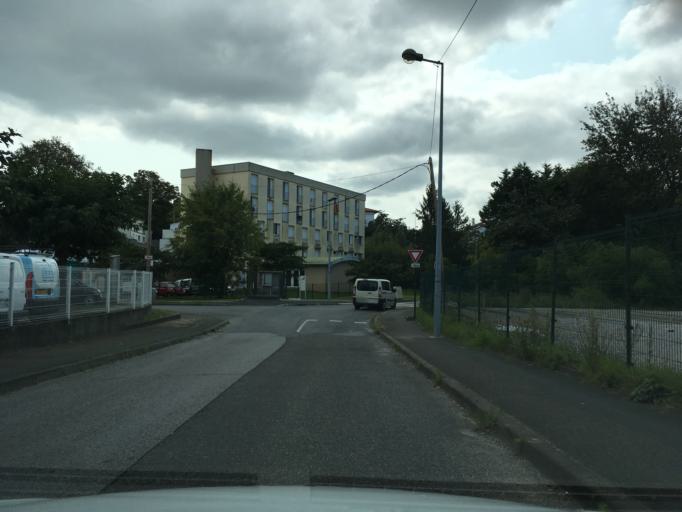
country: FR
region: Aquitaine
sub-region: Departement des Pyrenees-Atlantiques
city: Bayonne
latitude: 43.4857
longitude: -1.4993
